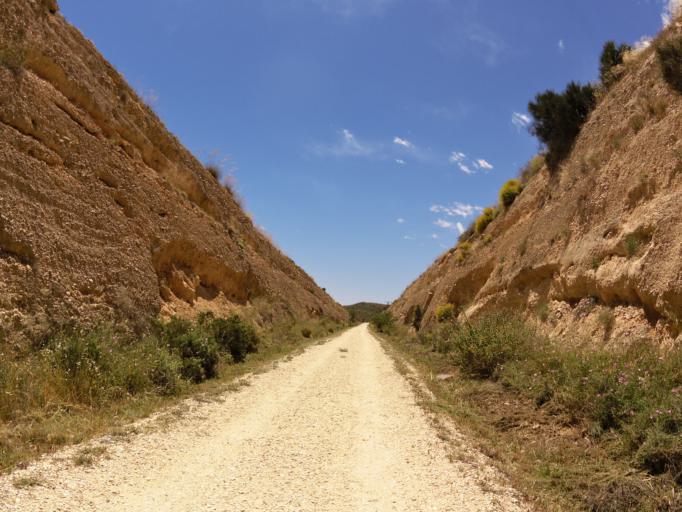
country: ES
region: Valencia
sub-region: Provincia de Alicante
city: Agost
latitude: 38.4498
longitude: -0.6739
